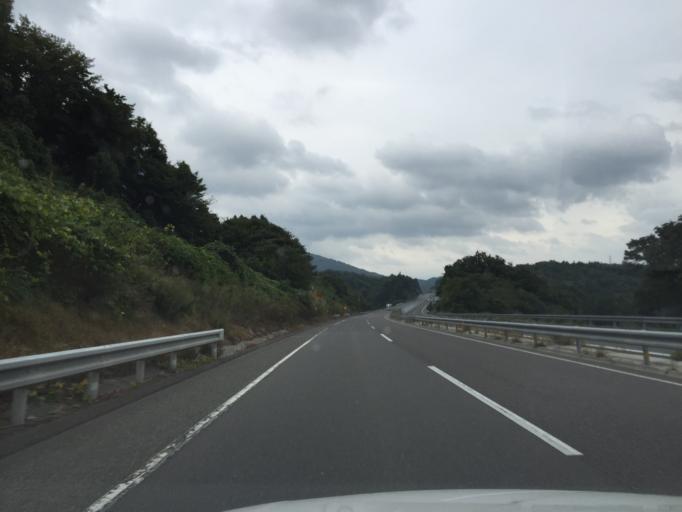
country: JP
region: Fukushima
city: Funehikimachi-funehiki
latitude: 37.4365
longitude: 140.5319
